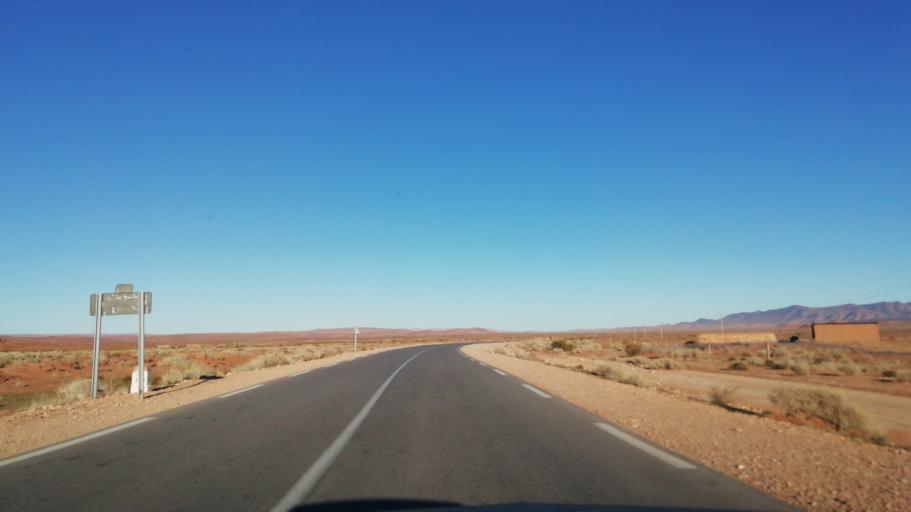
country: DZ
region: El Bayadh
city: El Abiodh Sidi Cheikh
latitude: 33.1720
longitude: 0.5177
